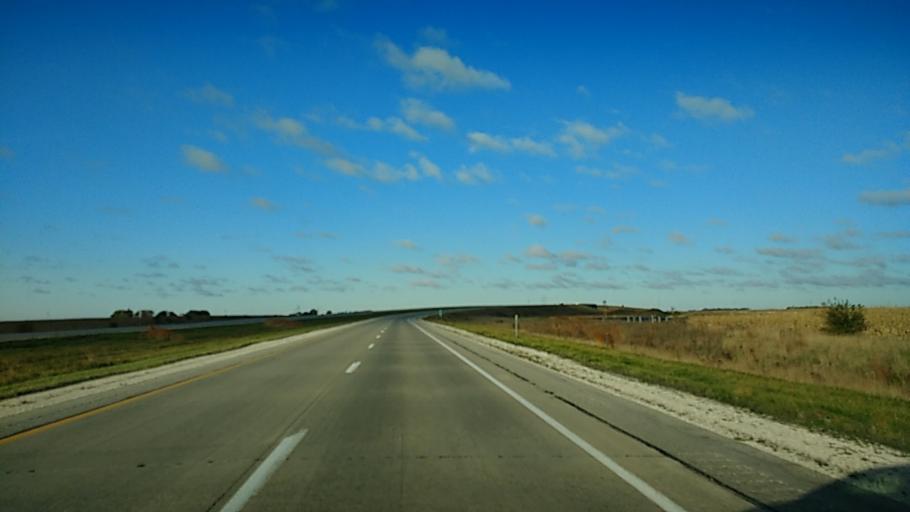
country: US
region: Iowa
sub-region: Calhoun County
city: Manson
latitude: 42.4468
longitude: -94.4646
